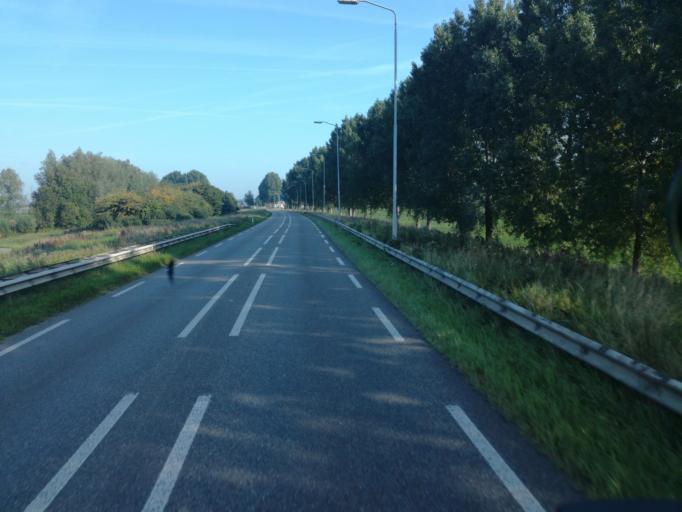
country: NL
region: North Brabant
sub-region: Gemeente Aalburg
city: Aalburg
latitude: 51.7411
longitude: 5.1158
